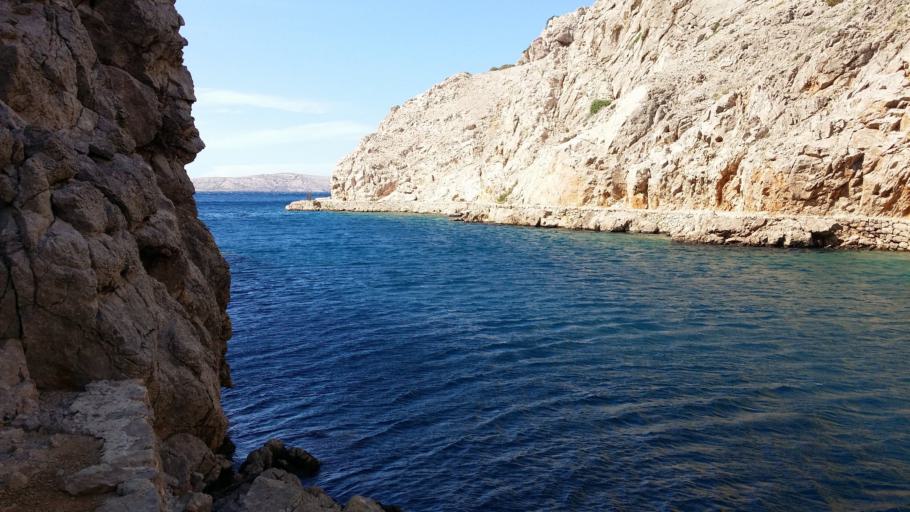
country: HR
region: Primorsko-Goranska
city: Banjol
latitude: 44.6996
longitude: 14.9006
